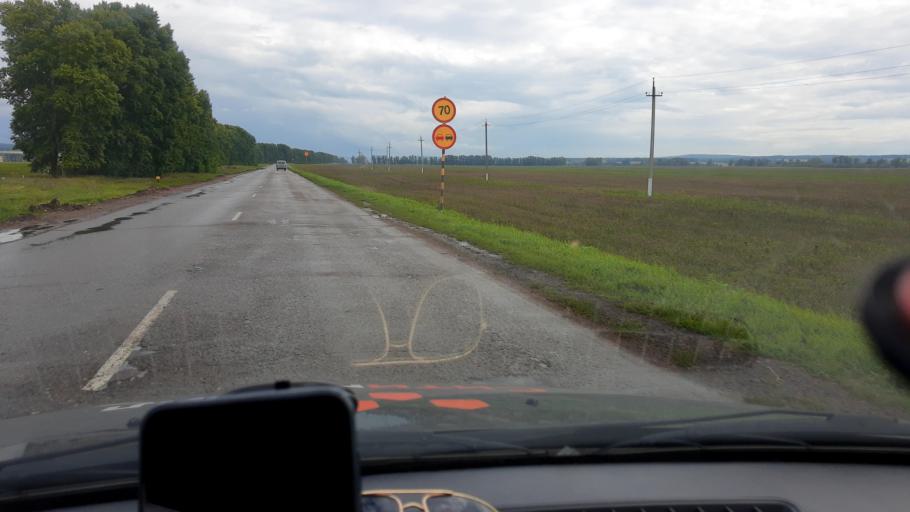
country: RU
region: Bashkortostan
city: Karmaskaly
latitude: 53.9741
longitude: 56.3889
